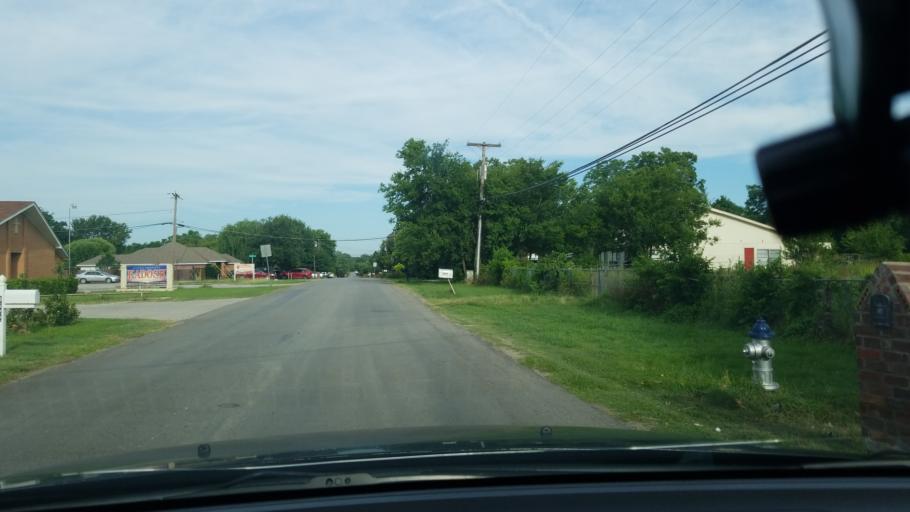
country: US
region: Texas
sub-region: Dallas County
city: Balch Springs
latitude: 32.7593
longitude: -96.6590
